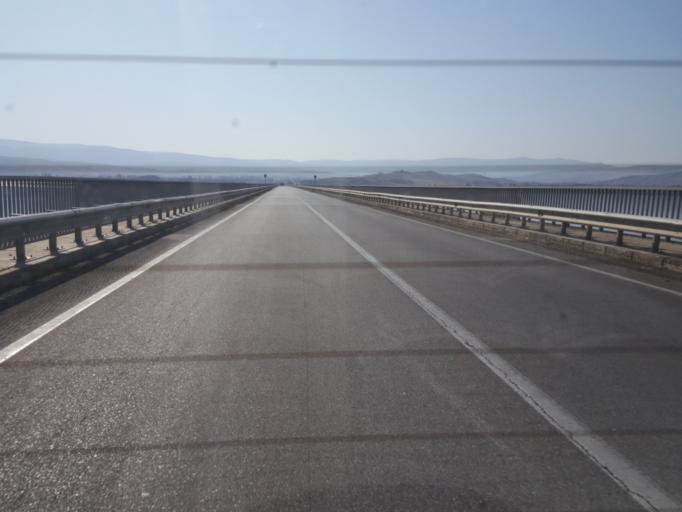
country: TR
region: Corum
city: Iskilip
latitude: 40.6265
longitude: 34.5660
